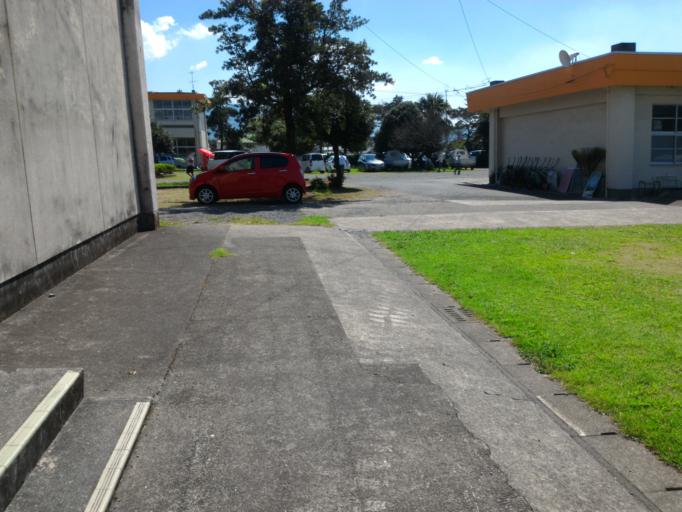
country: JP
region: Kagoshima
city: Kanoya
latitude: 31.3863
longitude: 130.9751
